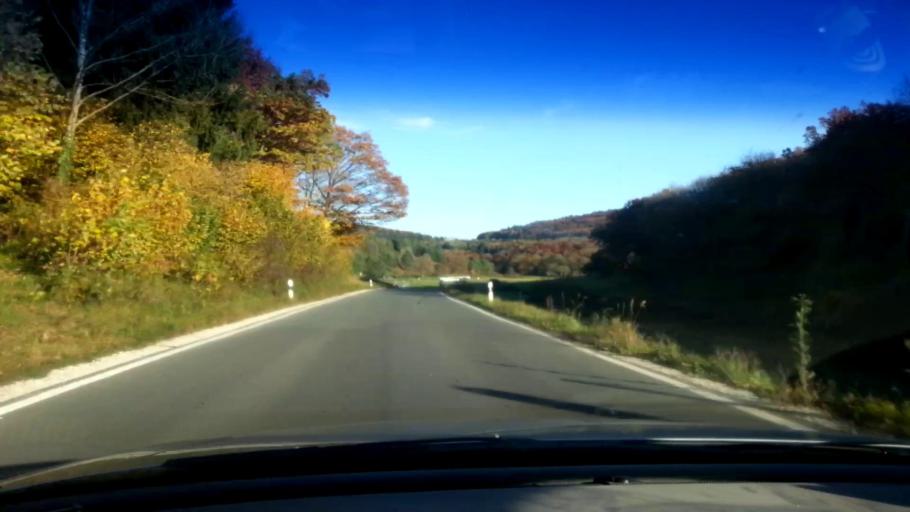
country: DE
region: Bavaria
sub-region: Upper Franconia
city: Poxdorf
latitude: 49.8905
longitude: 11.1207
